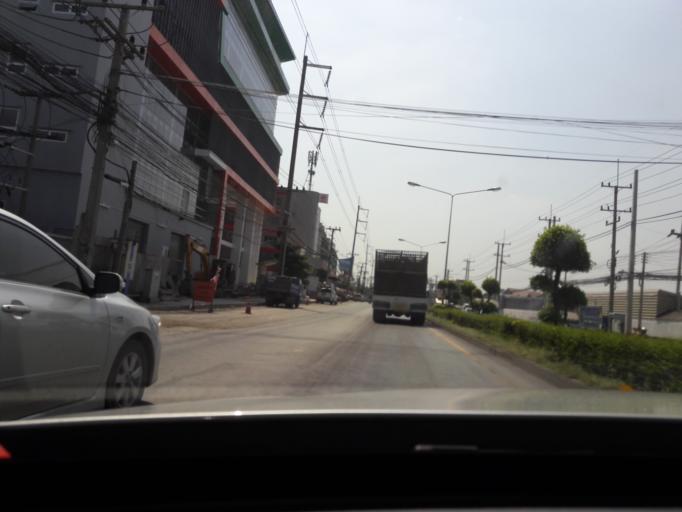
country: TH
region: Samut Sakhon
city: Samut Sakhon
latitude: 13.5811
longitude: 100.2769
